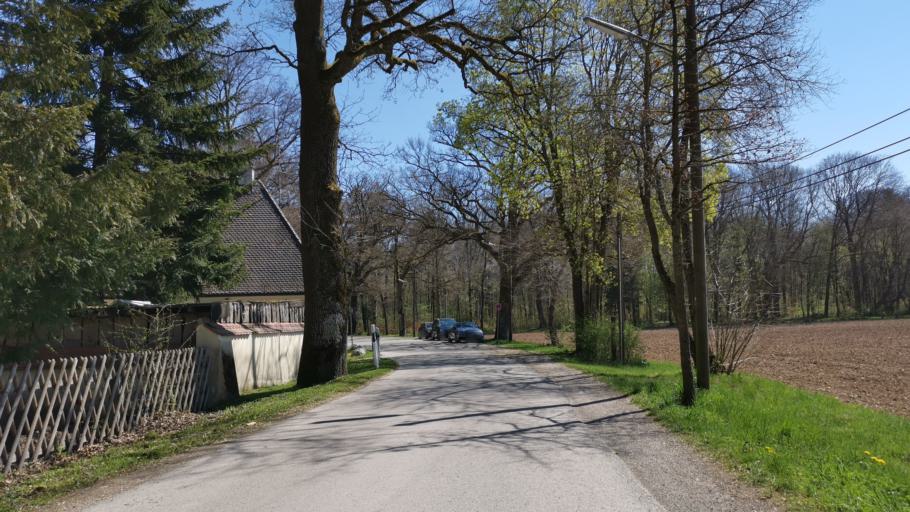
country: DE
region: Bavaria
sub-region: Upper Bavaria
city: Pullach im Isartal
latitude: 48.0680
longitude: 11.5129
